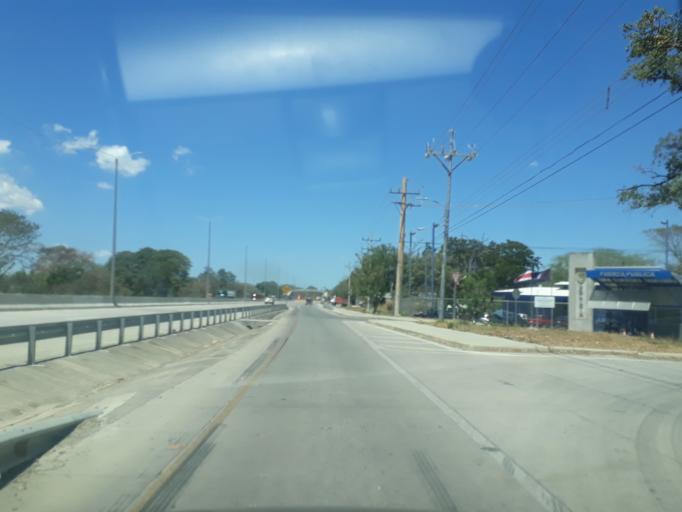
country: CR
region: Guanacaste
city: Liberia
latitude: 10.6340
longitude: -85.4482
